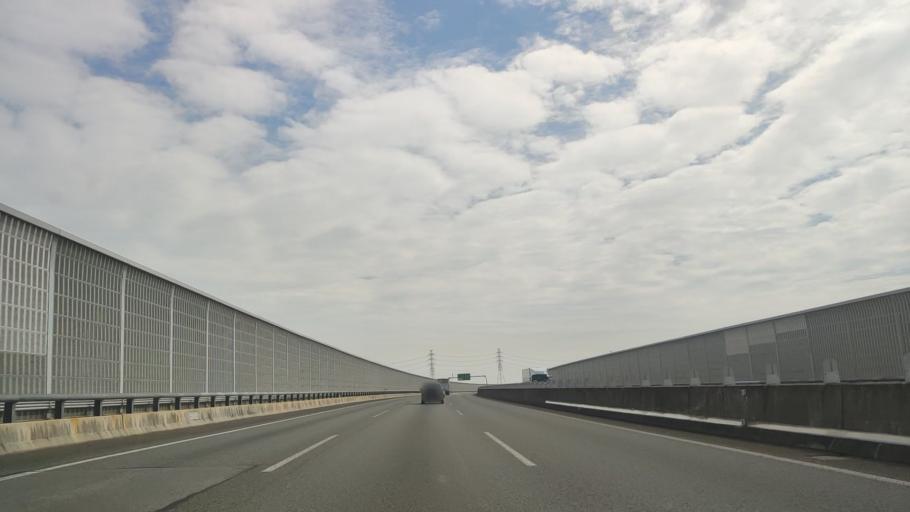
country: JP
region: Mie
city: Yokkaichi
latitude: 35.0289
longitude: 136.6719
